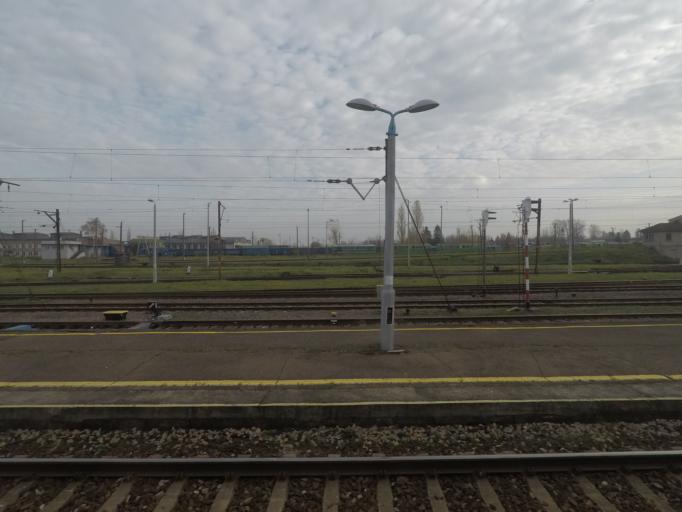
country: PL
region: Subcarpathian Voivodeship
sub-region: Powiat przemyski
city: Zurawica
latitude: 49.8333
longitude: 22.8380
